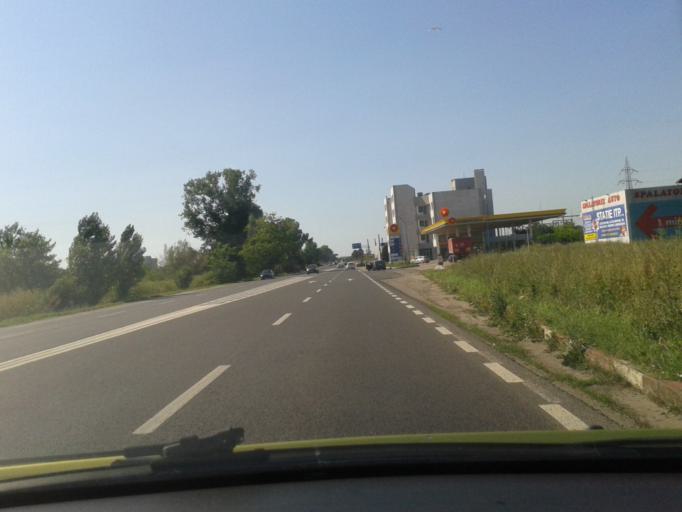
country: RO
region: Constanta
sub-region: Municipiul Mangalia
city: Mangalia
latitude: 43.8328
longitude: 28.5784
